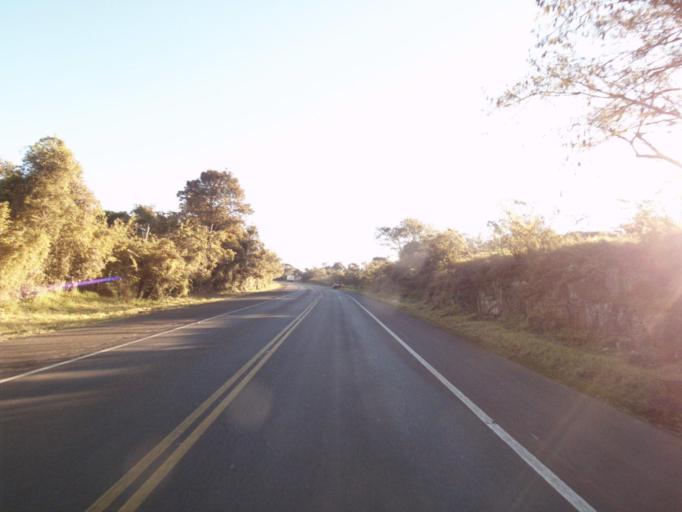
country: BR
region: Santa Catarina
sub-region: Chapeco
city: Chapeco
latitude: -26.8998
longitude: -52.8868
